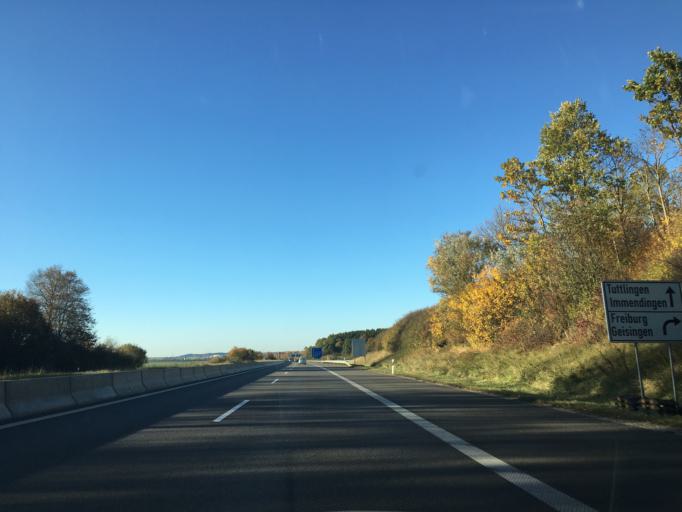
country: DE
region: Baden-Wuerttemberg
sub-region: Freiburg Region
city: Tuningen
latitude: 47.9795
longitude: 8.6163
